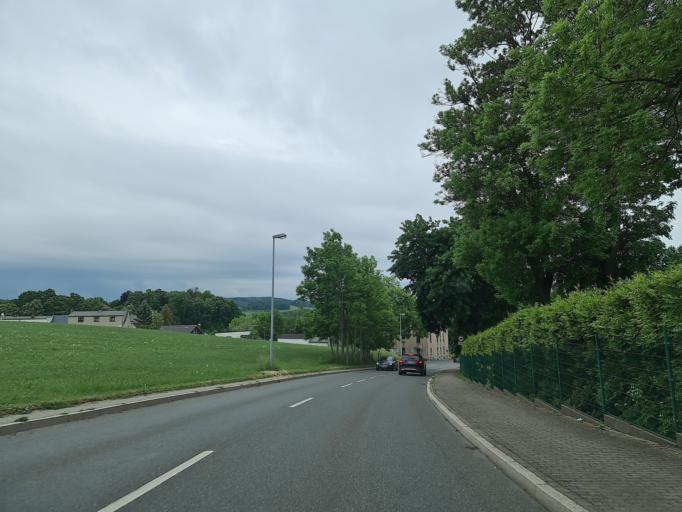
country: DE
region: Saxony
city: Treuen
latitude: 50.5406
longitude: 12.3118
